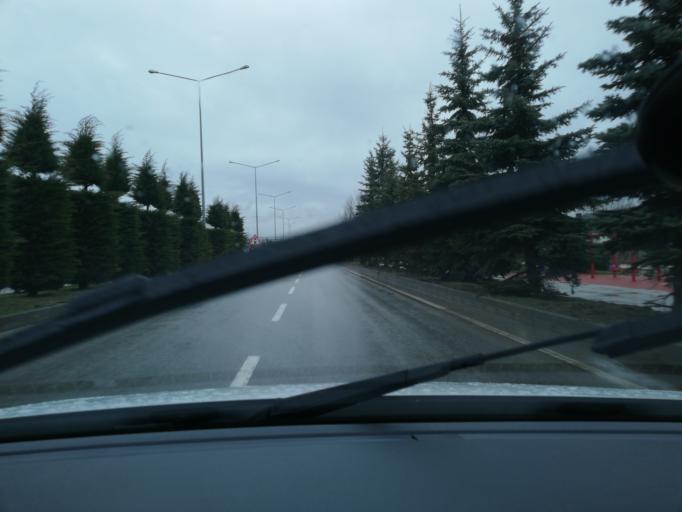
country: TR
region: Bolu
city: Bolu
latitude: 40.7211
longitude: 31.6133
